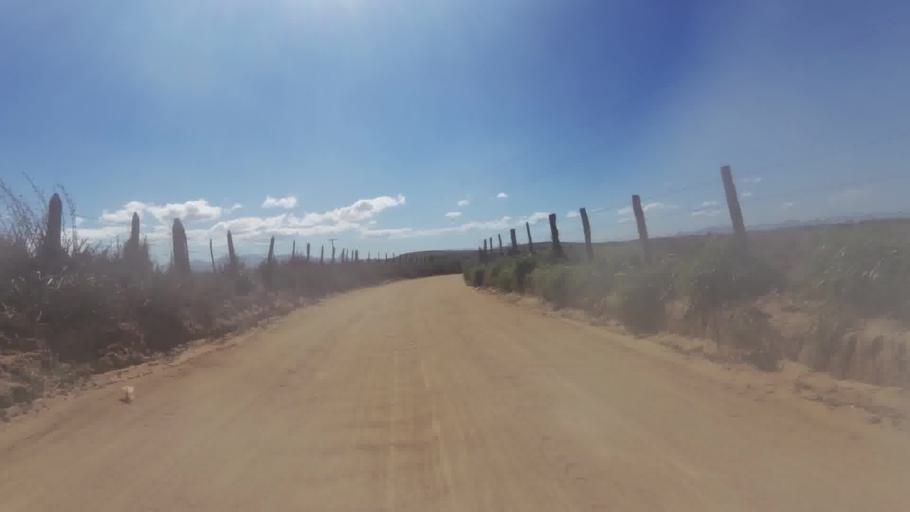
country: BR
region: Espirito Santo
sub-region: Marataizes
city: Marataizes
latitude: -21.1553
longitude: -40.9822
